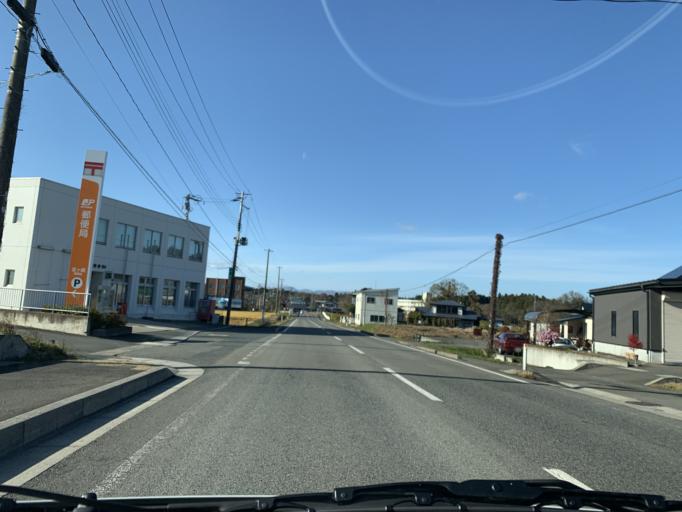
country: JP
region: Iwate
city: Mizusawa
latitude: 39.2035
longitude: 141.1141
